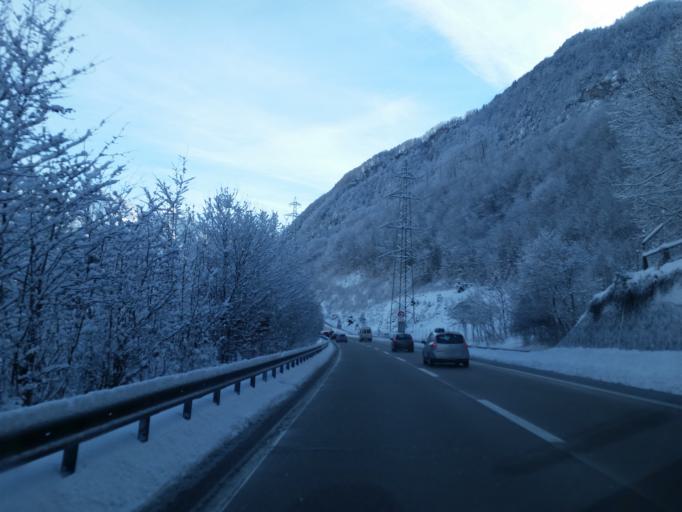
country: CH
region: Saint Gallen
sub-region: Wahlkreis Sarganserland
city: Quarten
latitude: 47.1107
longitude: 9.2738
